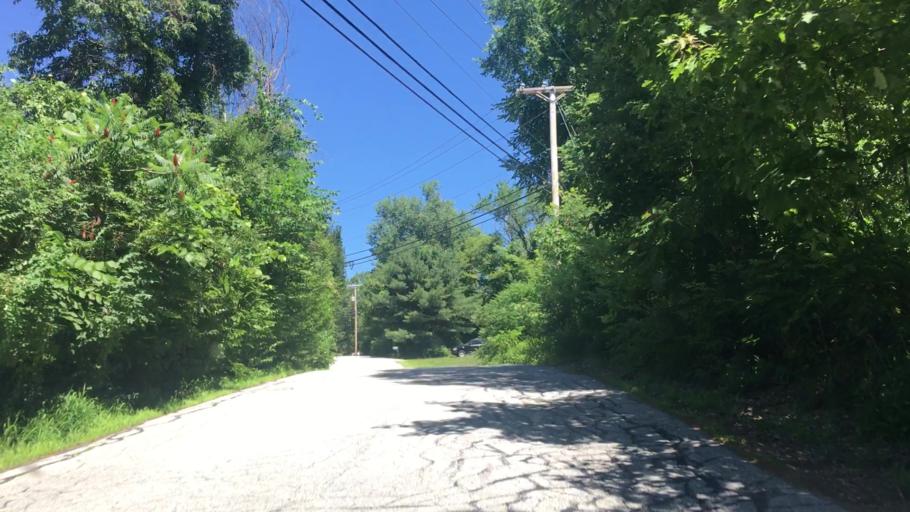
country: US
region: New Hampshire
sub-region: Merrimack County
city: Henniker
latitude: 43.1865
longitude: -71.7857
